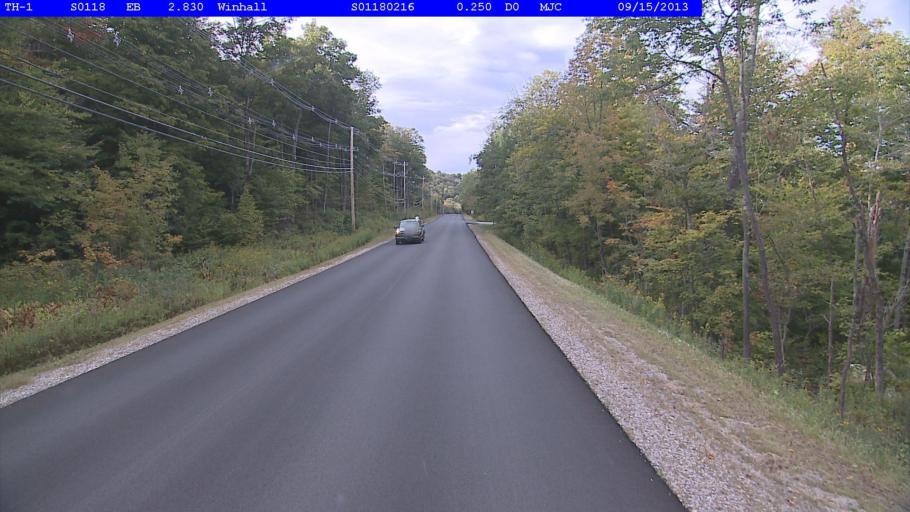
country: US
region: Vermont
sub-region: Bennington County
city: Manchester Center
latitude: 43.1188
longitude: -72.9110
